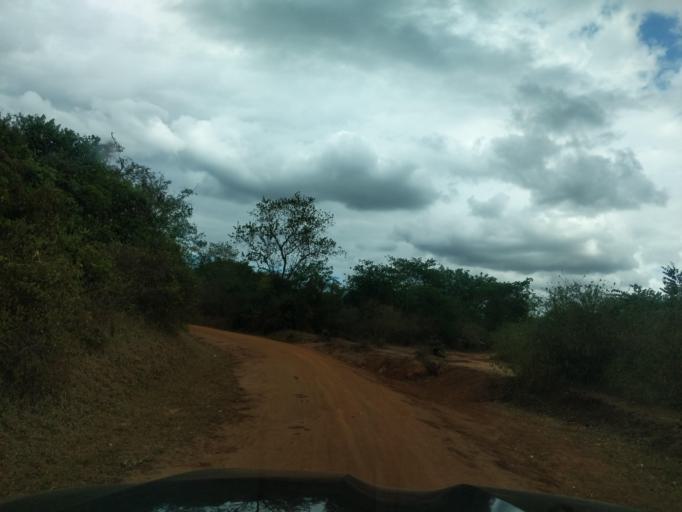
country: TZ
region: Pwani
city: Mvomero
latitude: -5.9394
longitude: 38.4213
